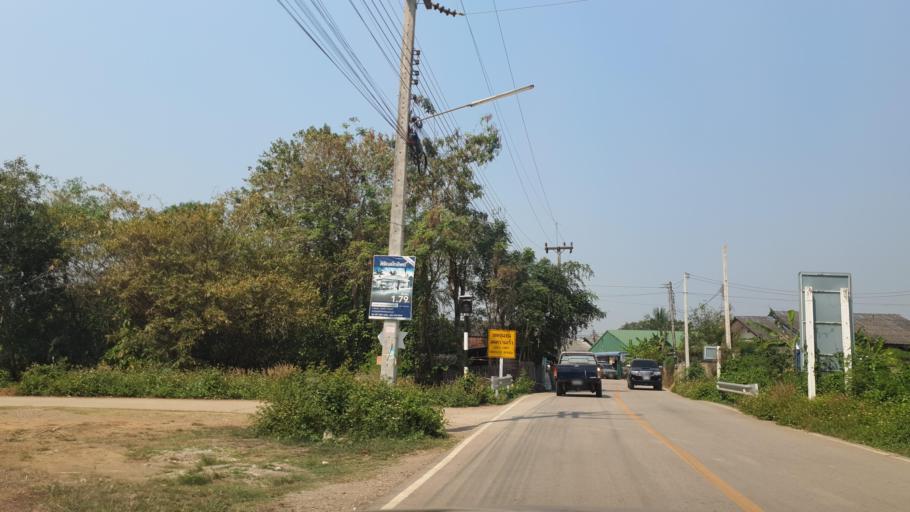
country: TH
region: Lamphun
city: Lamphun
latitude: 18.5525
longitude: 99.0743
